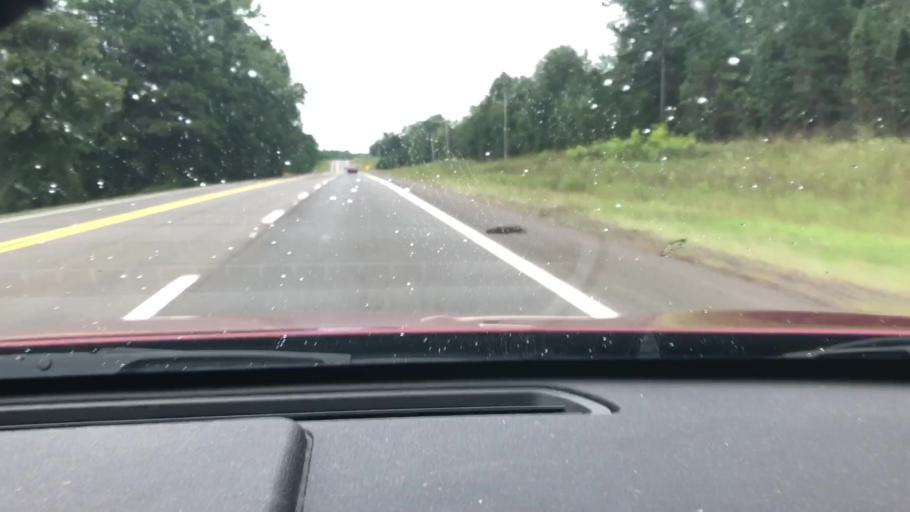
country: US
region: Arkansas
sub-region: Columbia County
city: Waldo
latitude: 33.3510
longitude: -93.3763
